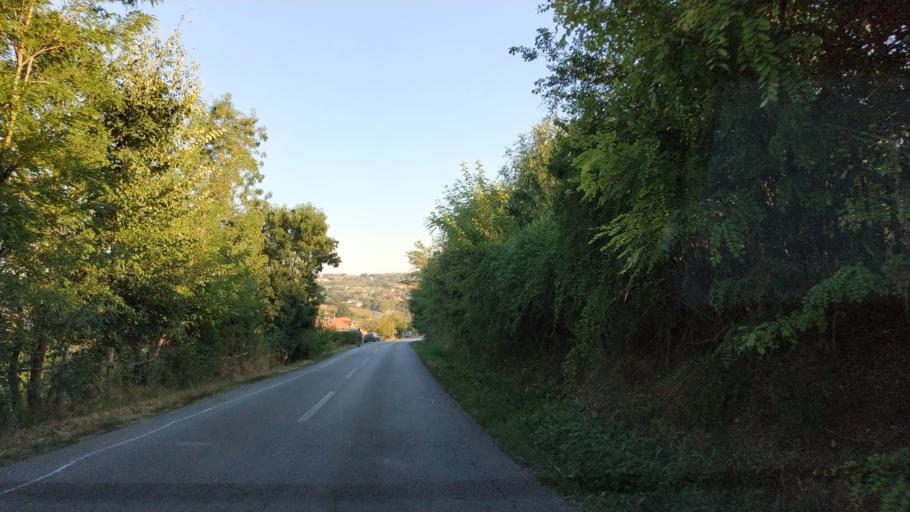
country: RS
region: Central Serbia
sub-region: Sumadijski Okrug
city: Arangelovac
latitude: 44.2807
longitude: 20.6199
